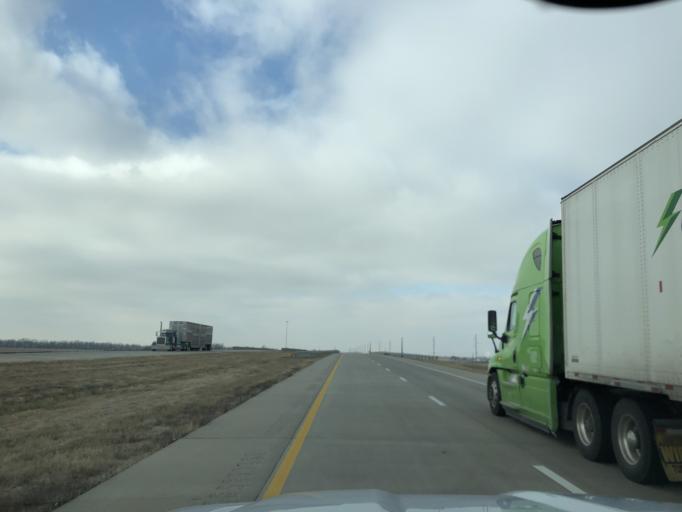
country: US
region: Kansas
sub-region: Reno County
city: Hutchinson
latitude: 38.0288
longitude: -97.8643
